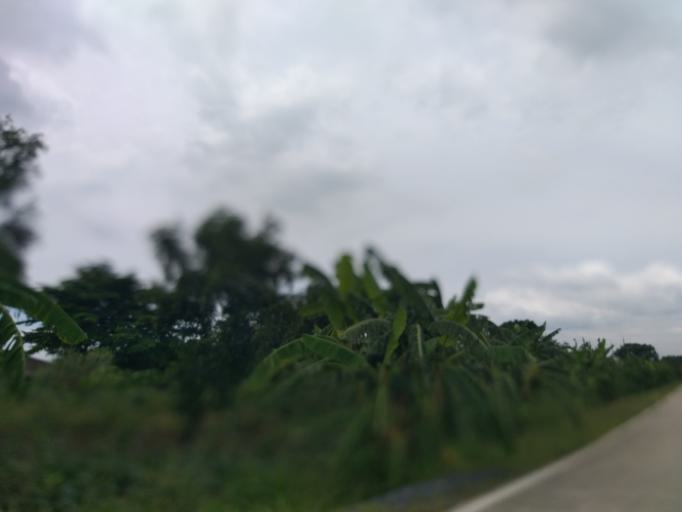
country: TH
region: Pathum Thani
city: Ban Lam Luk Ka
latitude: 13.9599
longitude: 100.8527
